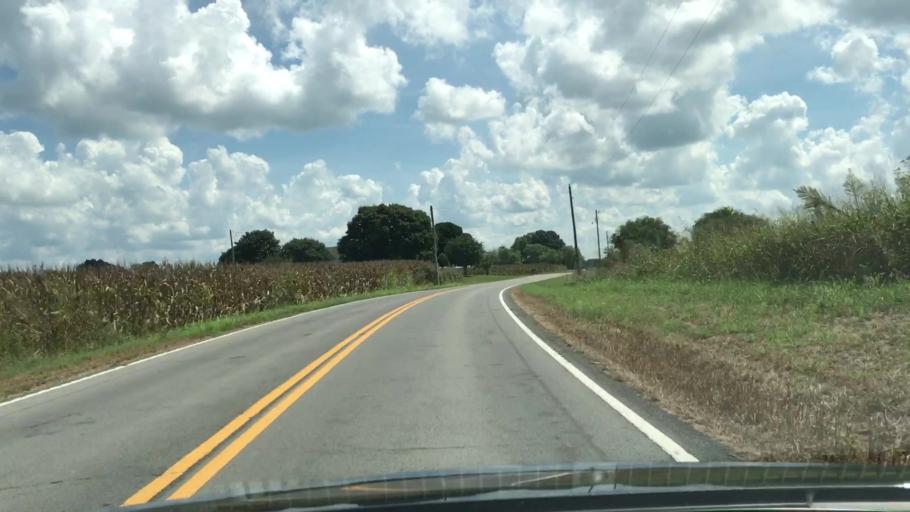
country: US
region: Tennessee
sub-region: Robertson County
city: Springfield
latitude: 36.5841
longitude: -86.8832
